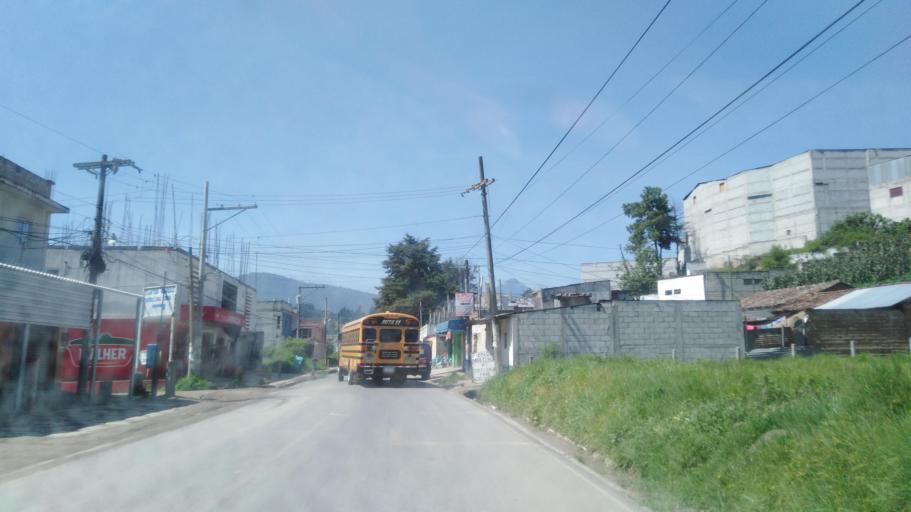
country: GT
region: Quetzaltenango
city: Quetzaltenango
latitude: 14.8557
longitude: -91.4914
